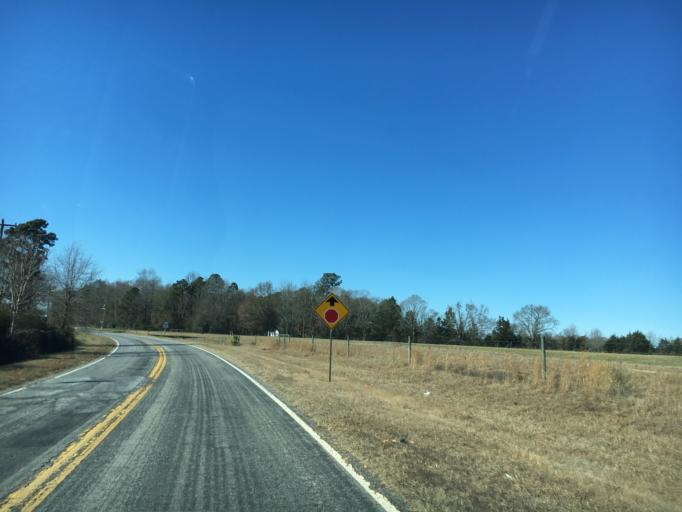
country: US
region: South Carolina
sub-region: Anderson County
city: Iva
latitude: 34.3779
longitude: -82.6978
